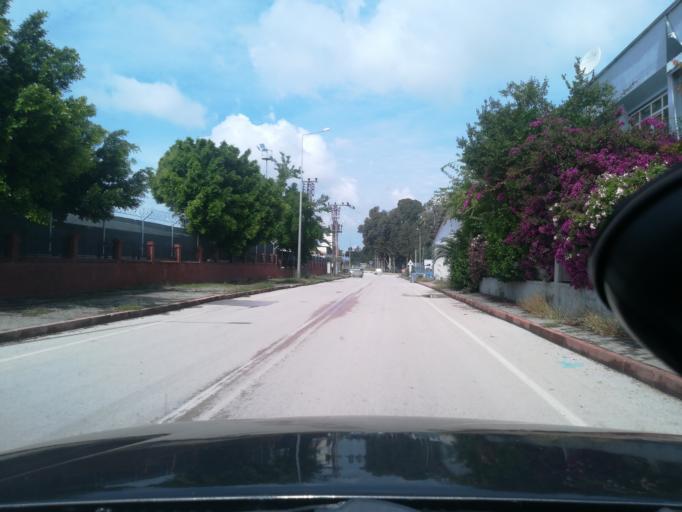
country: TR
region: Adana
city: Yuregir
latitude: 36.9848
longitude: 35.4329
